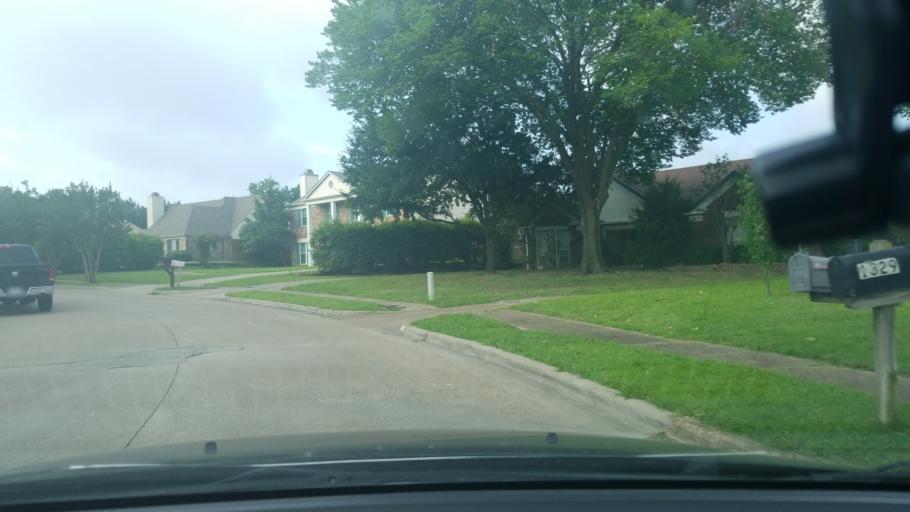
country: US
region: Texas
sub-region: Dallas County
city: Mesquite
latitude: 32.7871
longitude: -96.6512
